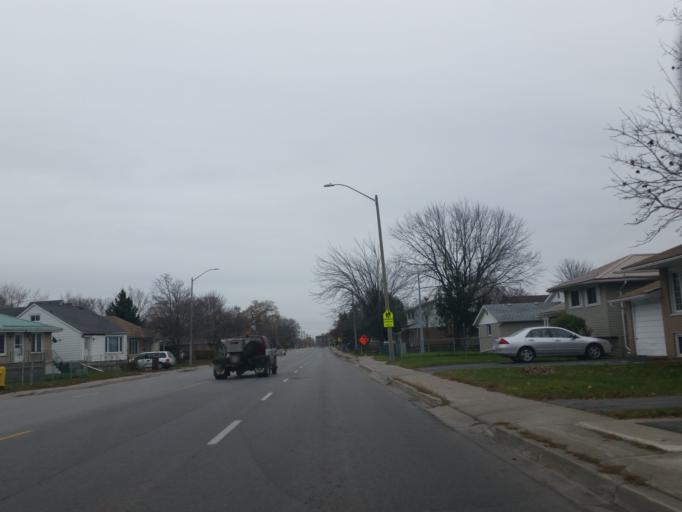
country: CA
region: Ontario
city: Quinte West
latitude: 44.1131
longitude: -77.5738
